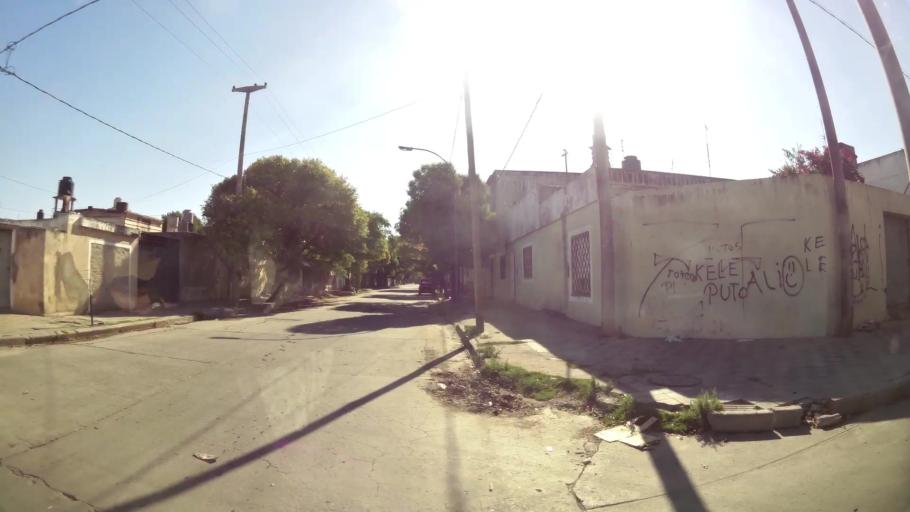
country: AR
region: Cordoba
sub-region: Departamento de Capital
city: Cordoba
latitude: -31.3979
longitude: -64.1526
